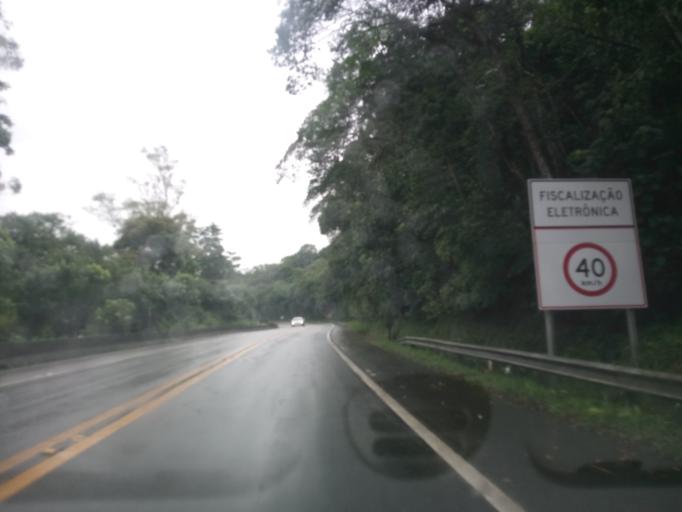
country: BR
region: Sao Paulo
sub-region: Sao Bernardo Do Campo
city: Sao Bernardo do Campo
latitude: -23.7839
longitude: -46.5075
